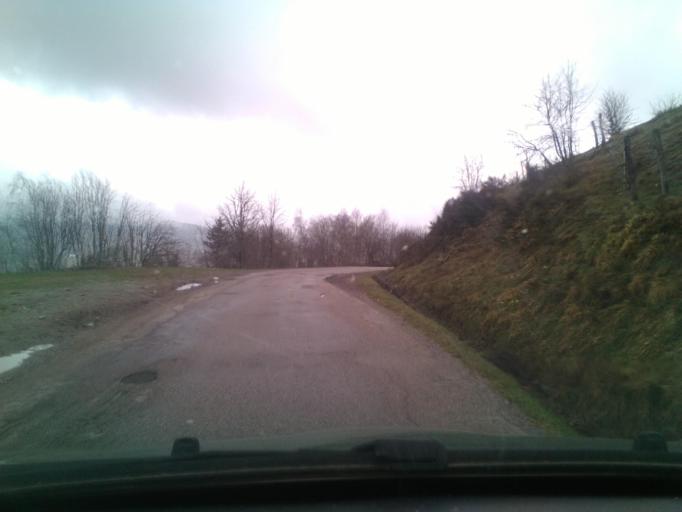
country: FR
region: Lorraine
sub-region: Departement des Vosges
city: La Bresse
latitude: 48.0208
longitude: 6.8830
